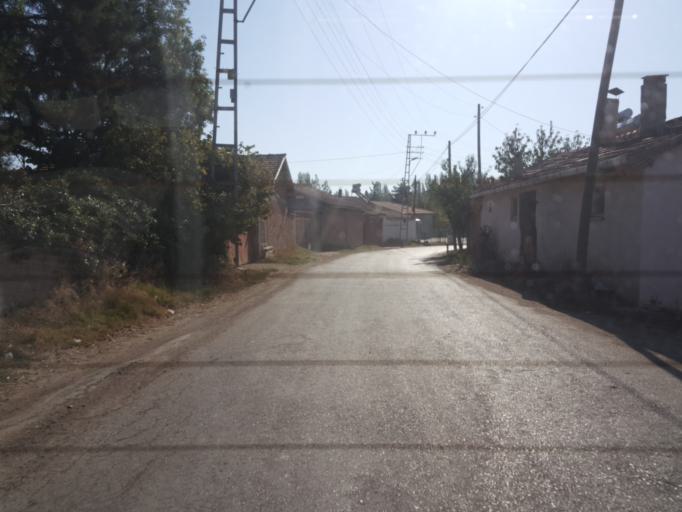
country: TR
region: Amasya
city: Saribugday
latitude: 40.7492
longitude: 35.4582
